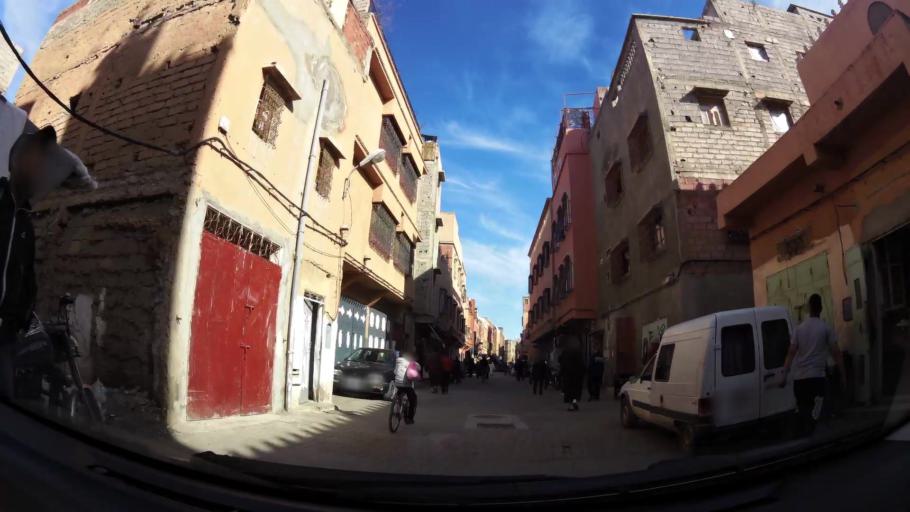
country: MA
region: Marrakech-Tensift-Al Haouz
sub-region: Marrakech
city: Marrakesh
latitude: 31.6132
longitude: -7.9615
